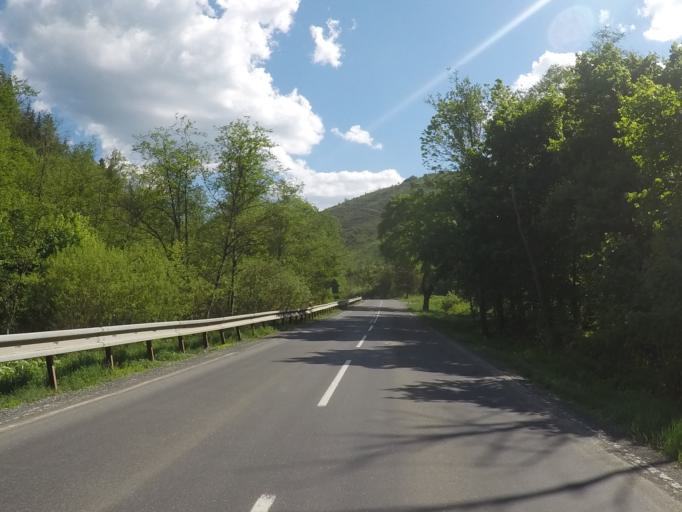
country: SK
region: Presovsky
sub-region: Okres Poprad
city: Poprad
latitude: 48.9640
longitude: 20.2924
